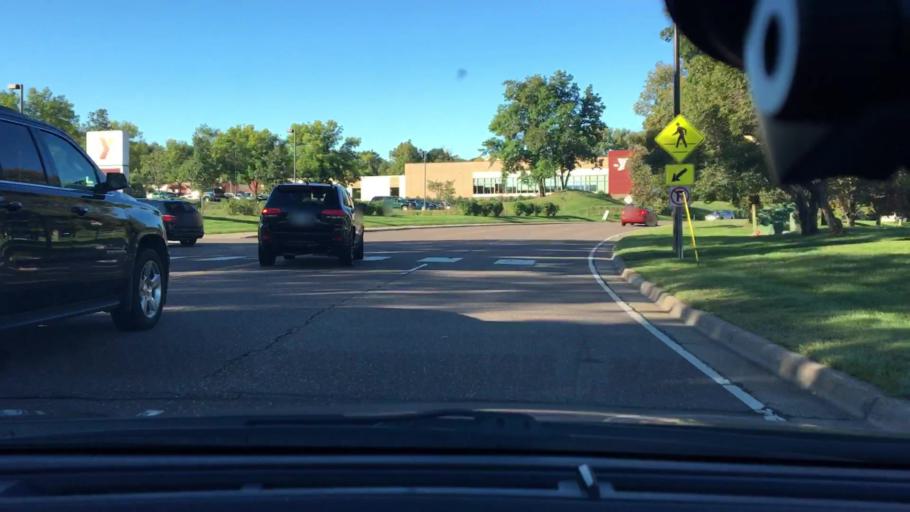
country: US
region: Minnesota
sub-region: Hennepin County
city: Minnetonka Mills
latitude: 44.9662
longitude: -93.4336
